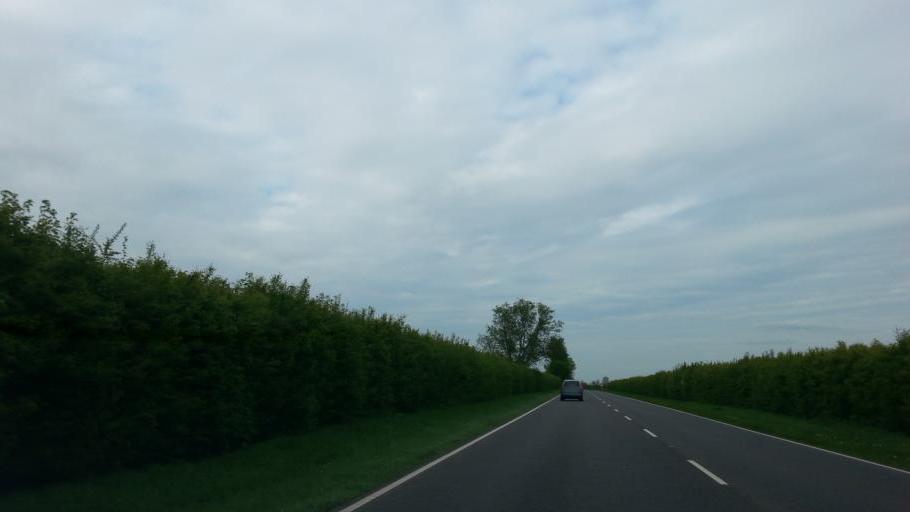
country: GB
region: England
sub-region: Cambridgeshire
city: Doddington
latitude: 52.4962
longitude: 0.0748
